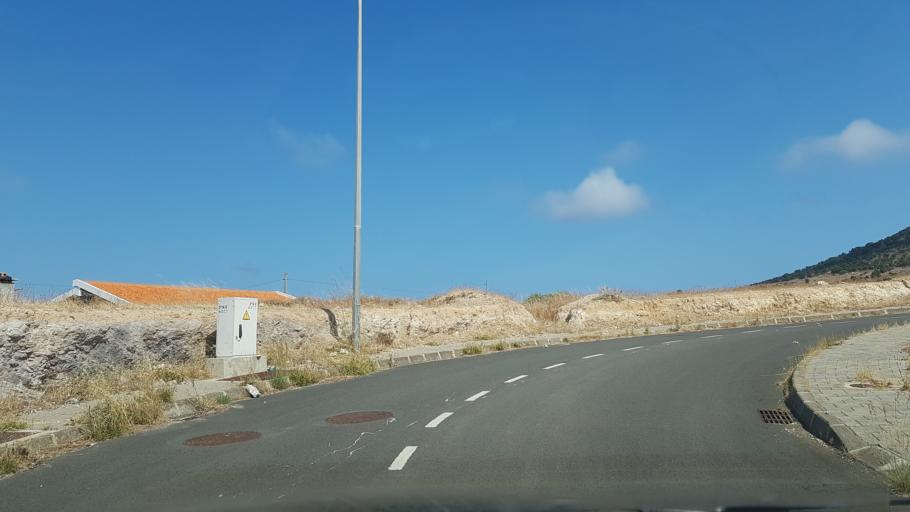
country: PT
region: Madeira
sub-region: Porto Santo
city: Vila de Porto Santo
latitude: 33.0645
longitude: -16.3302
